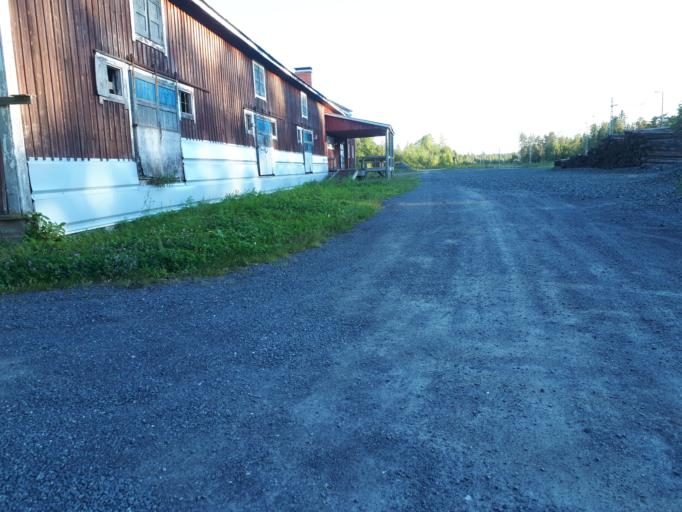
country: FI
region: Northern Ostrobothnia
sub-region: Oulunkaari
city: Ii
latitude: 65.3196
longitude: 25.4427
